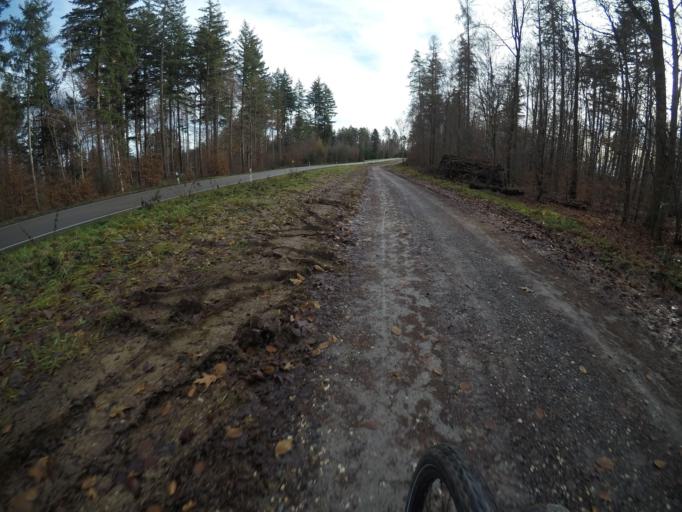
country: DE
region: Baden-Wuerttemberg
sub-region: Regierungsbezirk Stuttgart
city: Winterbach
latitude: 48.7718
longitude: 9.4735
